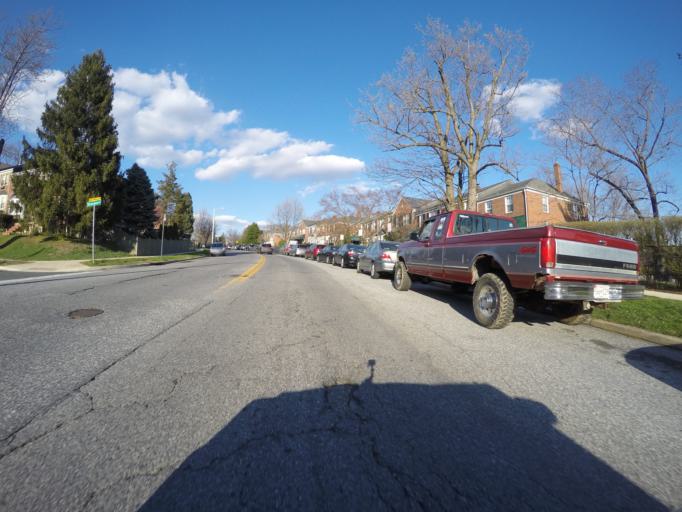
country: US
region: Maryland
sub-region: Baltimore County
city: Towson
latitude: 39.3814
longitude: -76.6187
